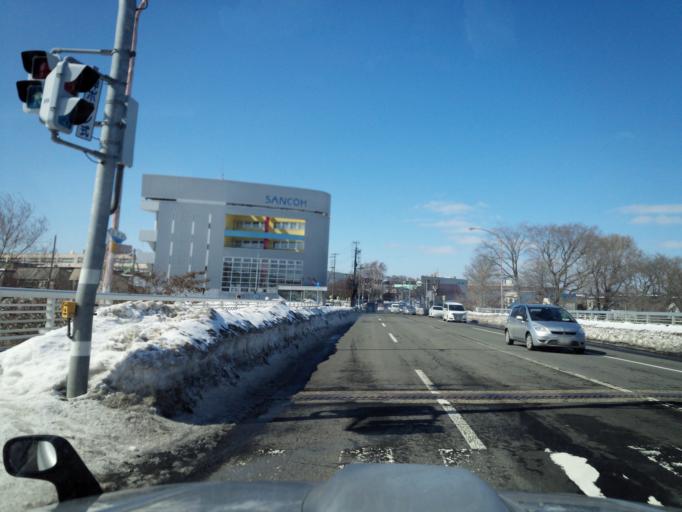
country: JP
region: Hokkaido
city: Sapporo
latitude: 43.0086
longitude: 141.4392
